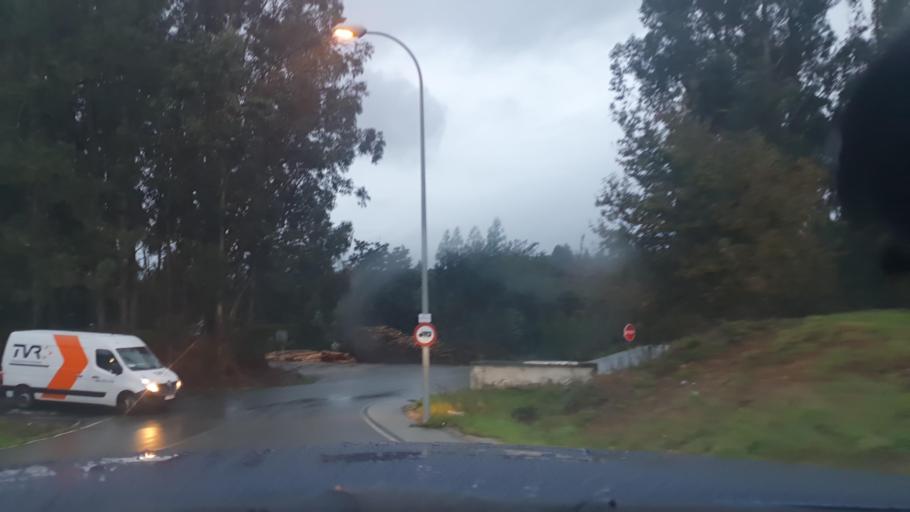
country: ES
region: Galicia
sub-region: Provincia da Coruna
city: Santiago de Compostela
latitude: 42.8532
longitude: -8.5863
